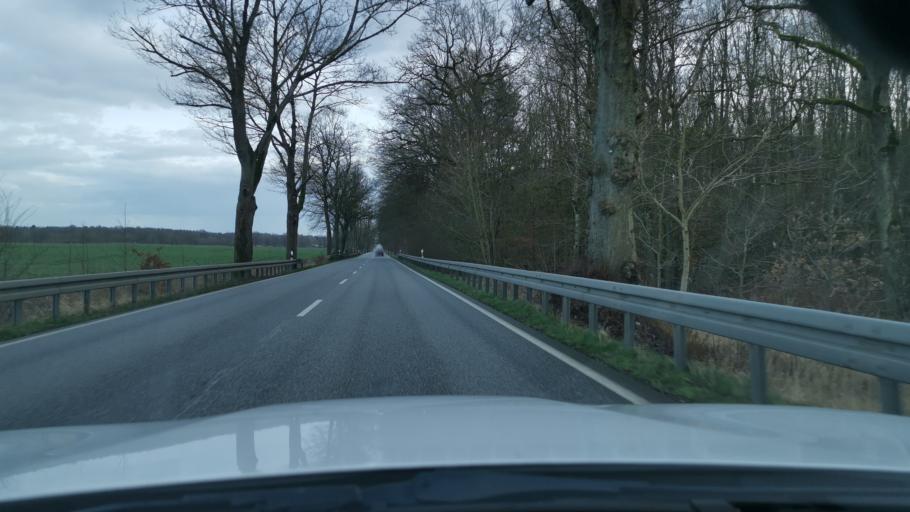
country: DE
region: Mecklenburg-Vorpommern
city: Dummerstorf
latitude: 54.0037
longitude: 12.2583
